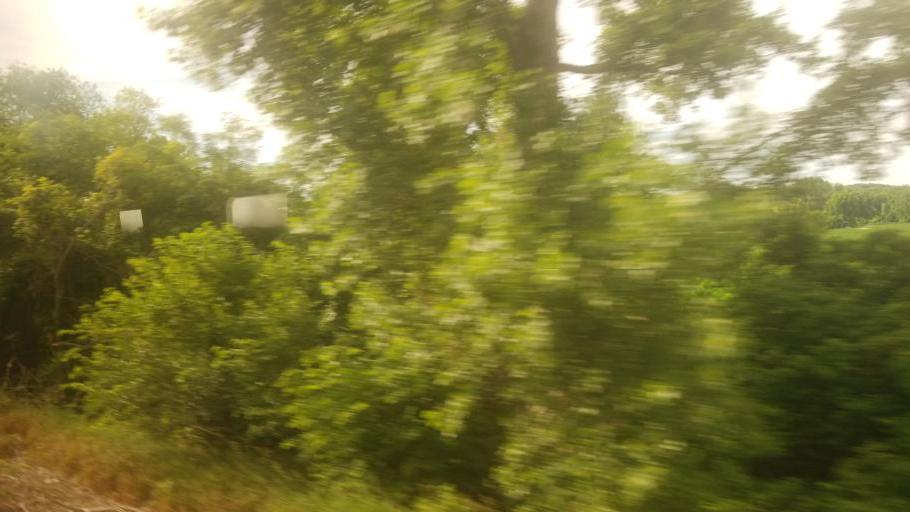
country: US
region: Kansas
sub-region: Douglas County
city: Lawrence
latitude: 39.0229
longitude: -95.3114
